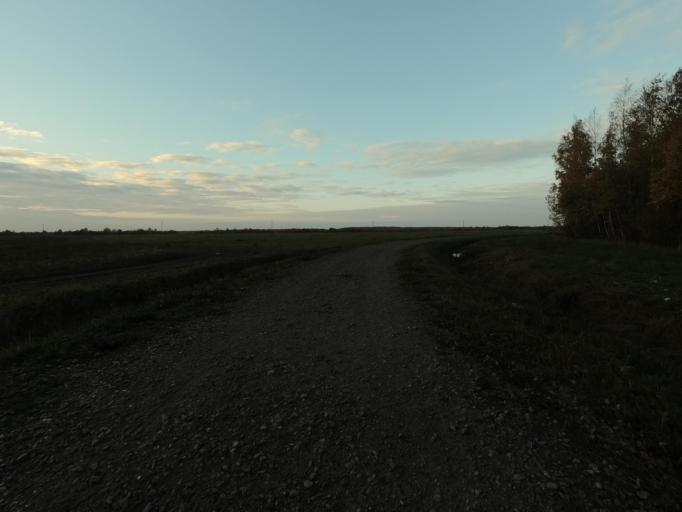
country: RU
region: Leningrad
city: Mga
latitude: 59.7830
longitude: 31.1960
